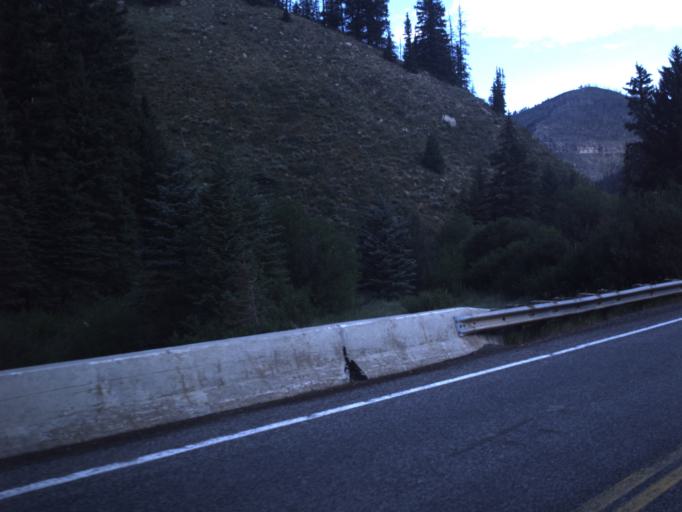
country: US
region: Utah
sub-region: Emery County
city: Huntington
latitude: 39.5231
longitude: -111.1543
